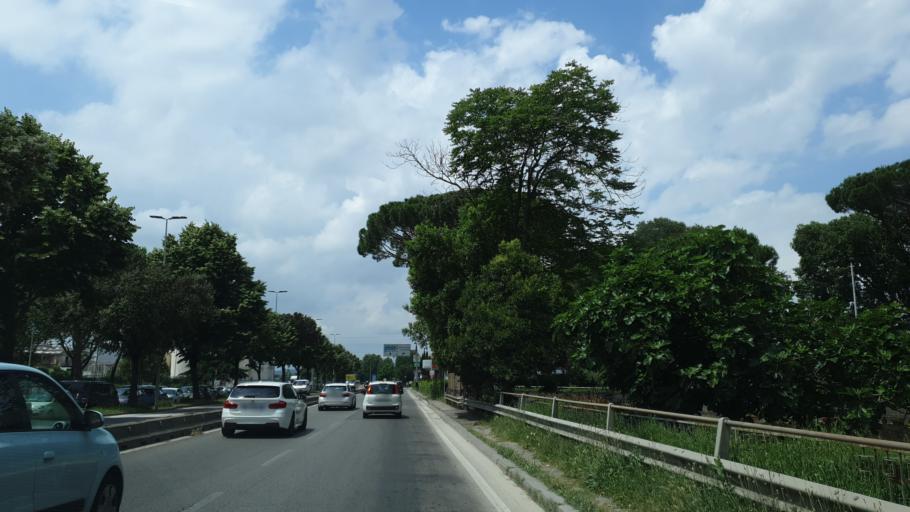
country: IT
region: Tuscany
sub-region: Province of Florence
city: Scandicci
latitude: 43.7728
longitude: 11.2017
